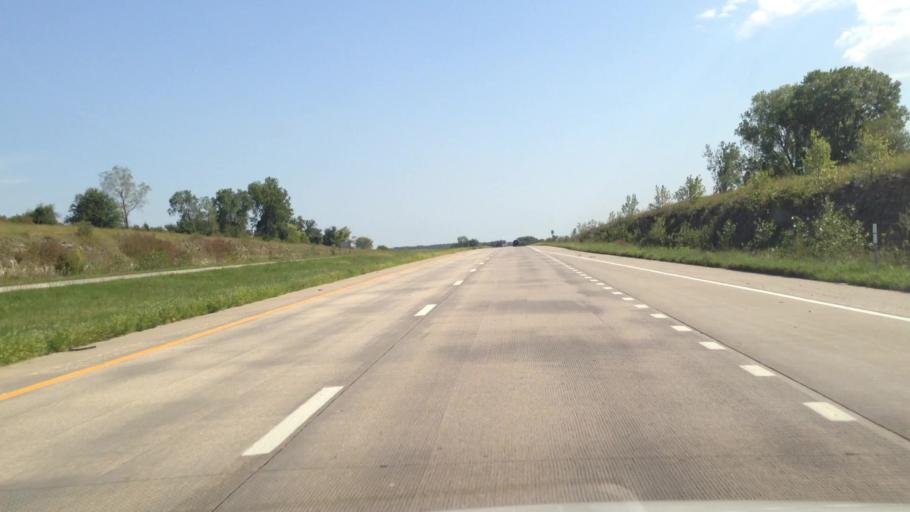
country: US
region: Kansas
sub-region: Miami County
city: Louisburg
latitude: 38.5583
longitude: -94.6922
